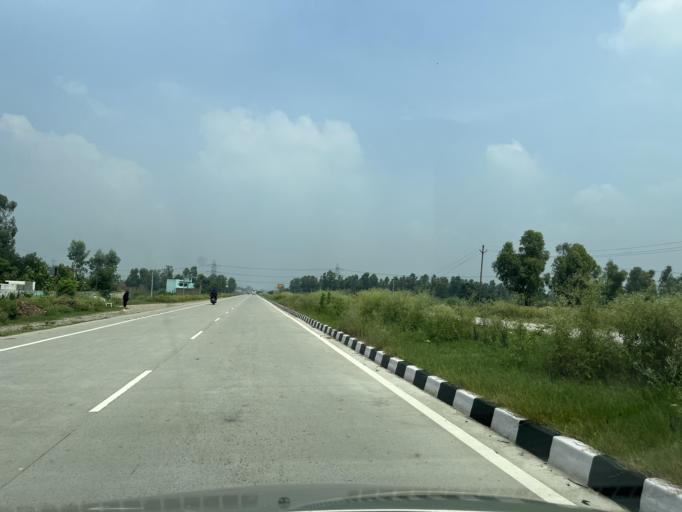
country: IN
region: Uttar Pradesh
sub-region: Bijnor
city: Najibabad
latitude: 29.5555
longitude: 78.3390
